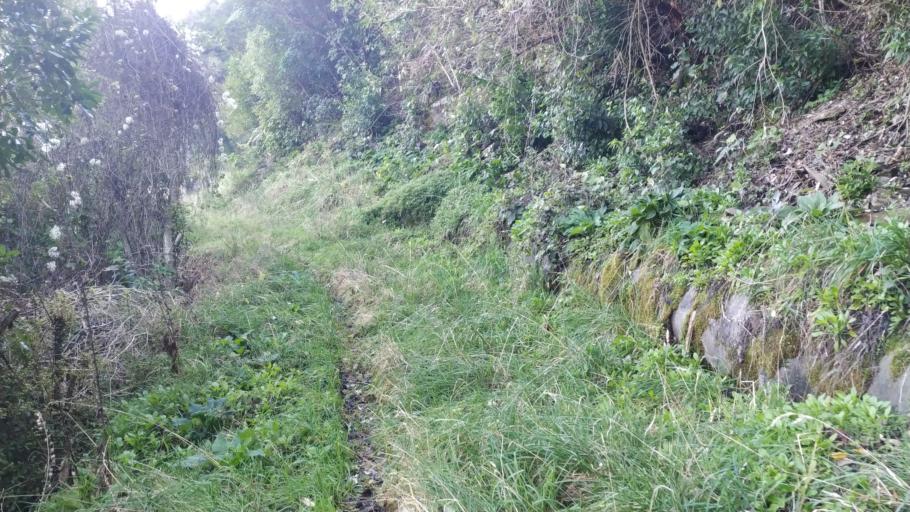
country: NZ
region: Nelson
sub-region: Nelson City
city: Nelson
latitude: -41.2934
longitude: 173.3365
